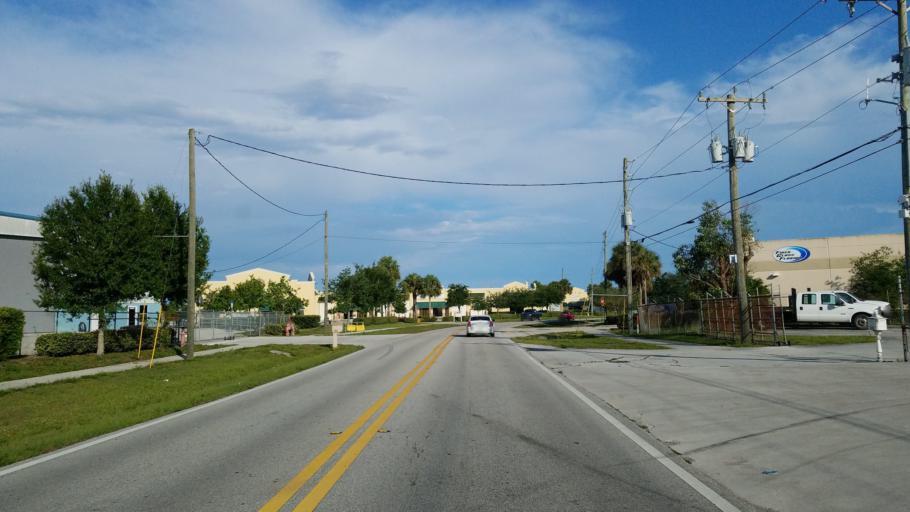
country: US
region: Florida
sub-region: Martin County
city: Port Salerno
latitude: 27.1512
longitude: -80.2067
